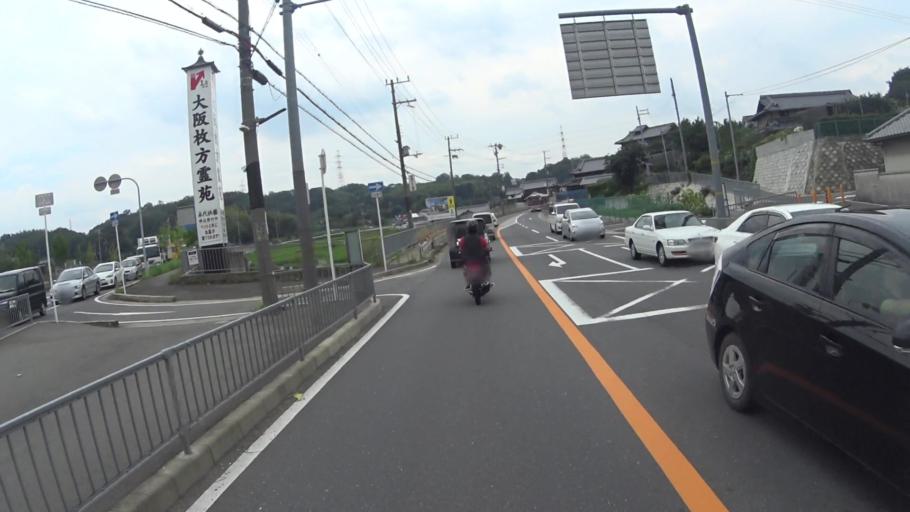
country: JP
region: Kyoto
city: Tanabe
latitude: 34.8127
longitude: 135.7192
